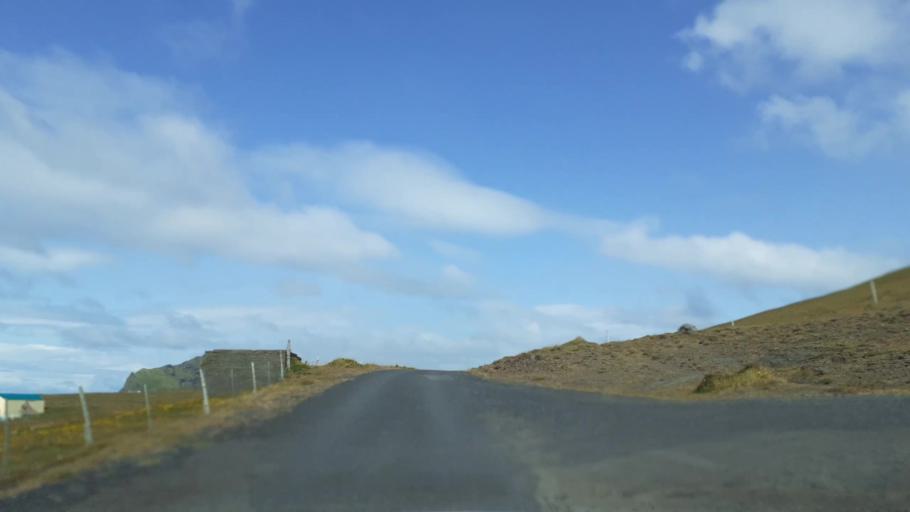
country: IS
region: South
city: Vestmannaeyjar
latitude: 63.4161
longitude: -20.2810
